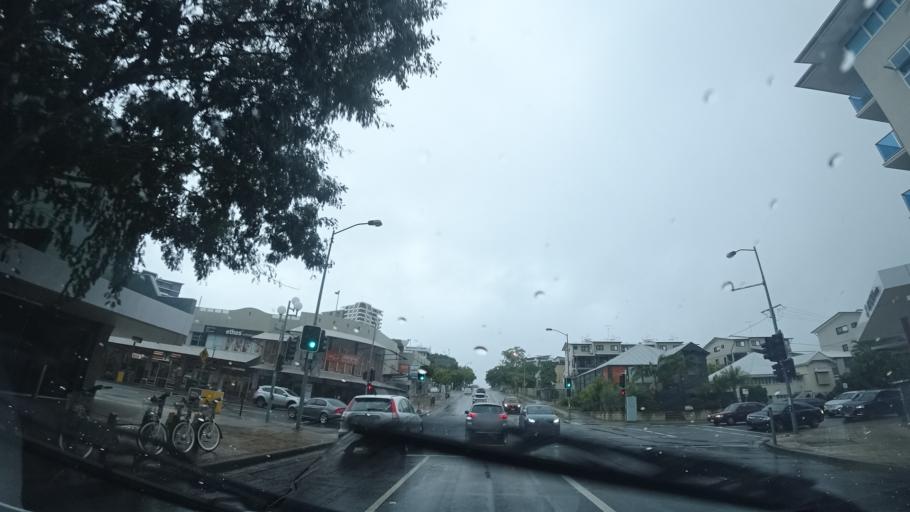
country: AU
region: Queensland
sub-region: Brisbane
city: Toowong
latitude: -27.4850
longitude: 152.9906
